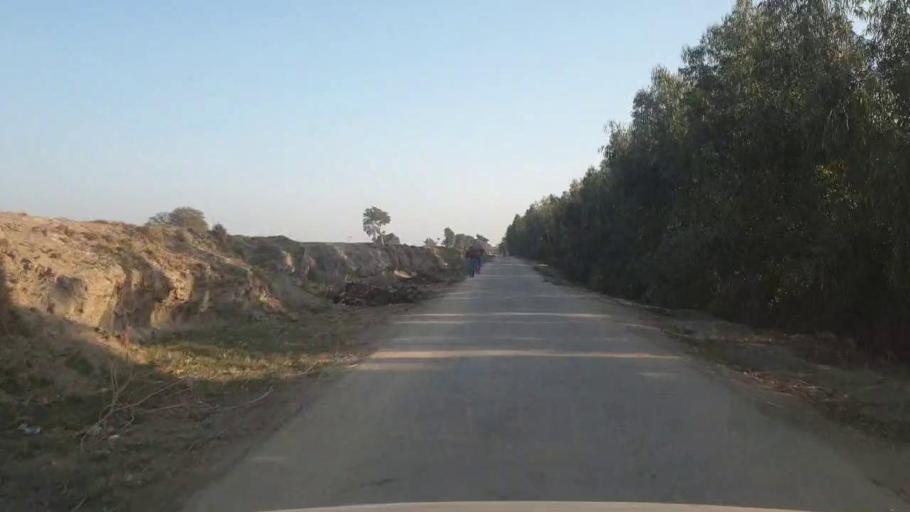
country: PK
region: Sindh
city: Chambar
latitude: 25.2916
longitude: 68.8944
